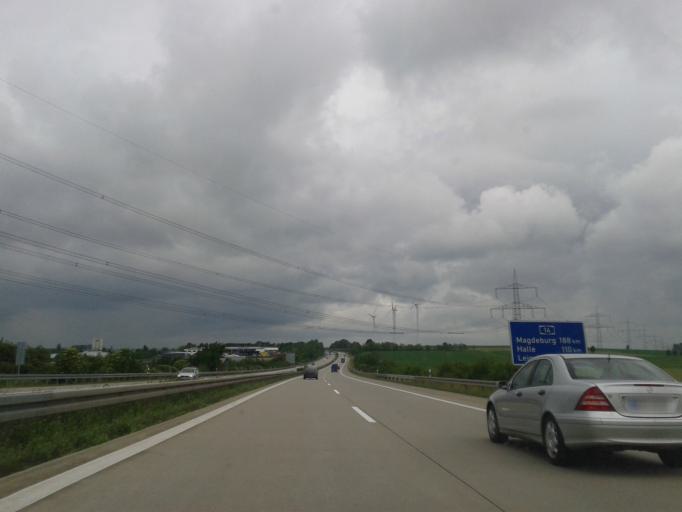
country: DE
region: Saxony
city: Mochau
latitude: 51.1168
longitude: 13.1733
